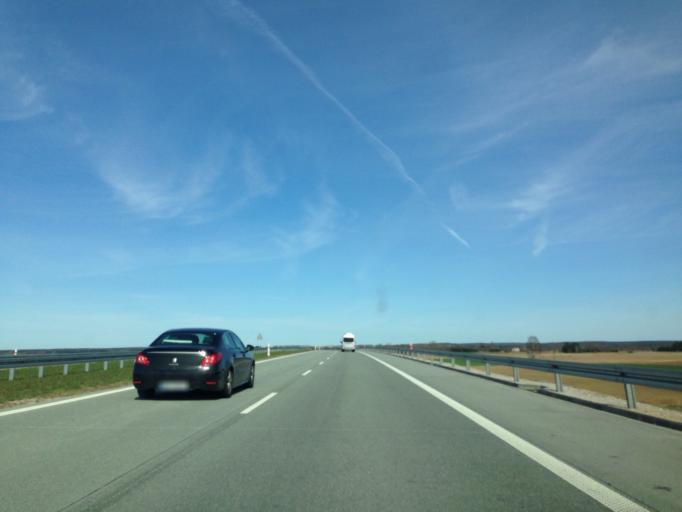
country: PL
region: Lodz Voivodeship
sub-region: Powiat sieradzki
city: Sieradz
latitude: 51.5673
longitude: 18.7769
